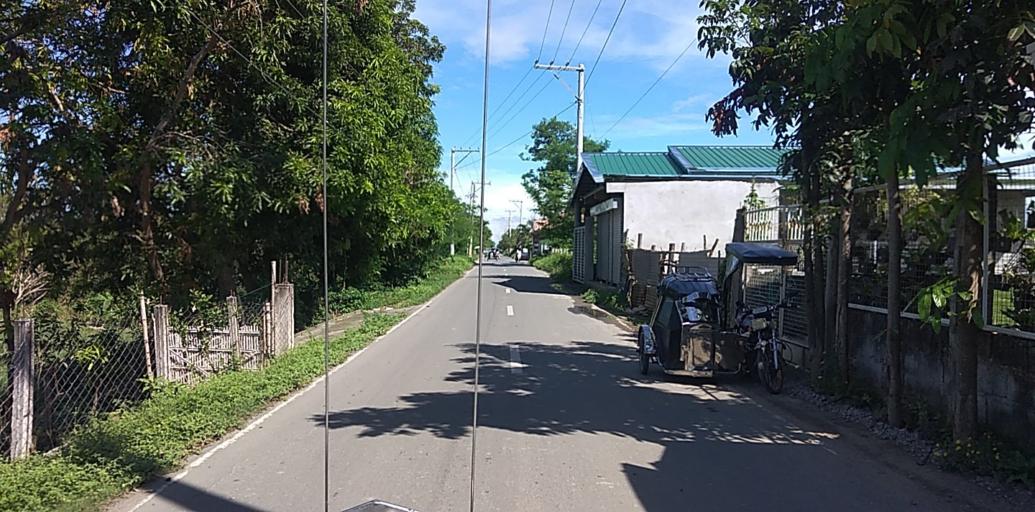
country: PH
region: Central Luzon
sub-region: Province of Pampanga
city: Candaba
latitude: 15.0827
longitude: 120.8094
